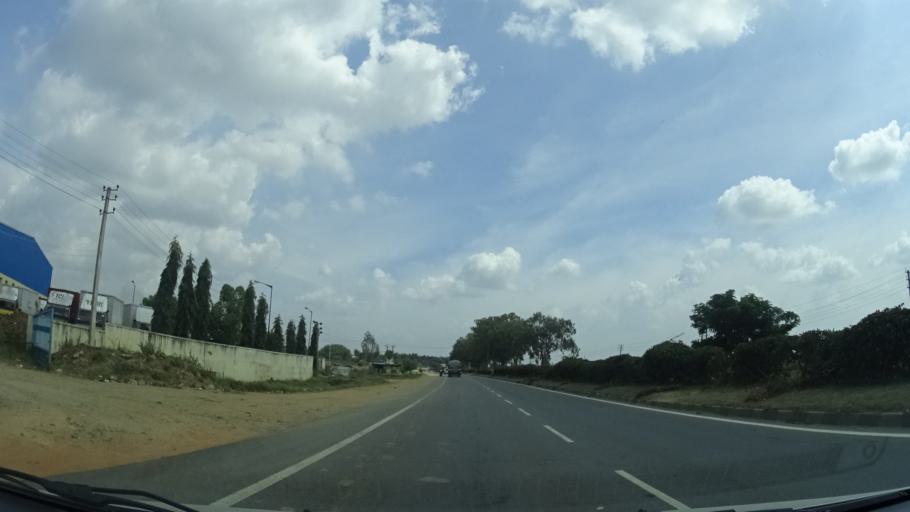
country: IN
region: Karnataka
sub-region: Bangalore Rural
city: Nelamangala
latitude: 13.1545
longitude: 77.3311
